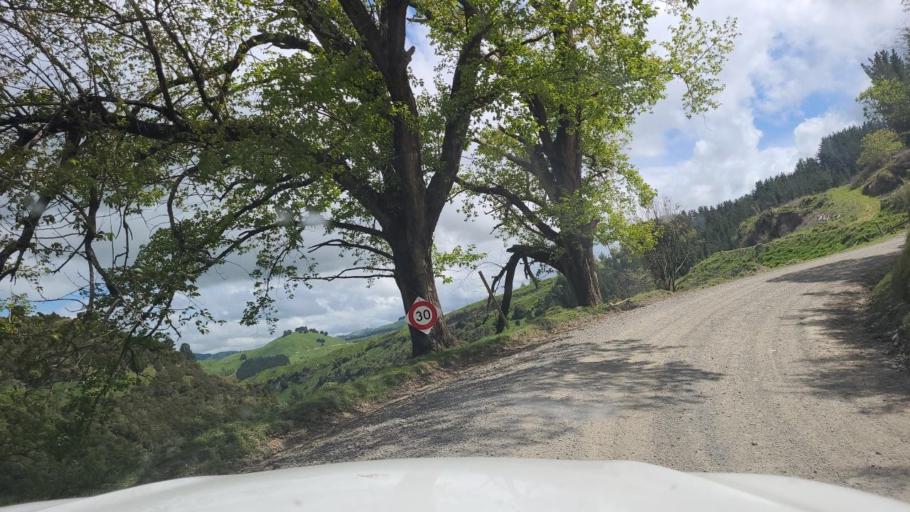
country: NZ
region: Hawke's Bay
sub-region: Napier City
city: Taradale
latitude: -39.2682
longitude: 176.6588
